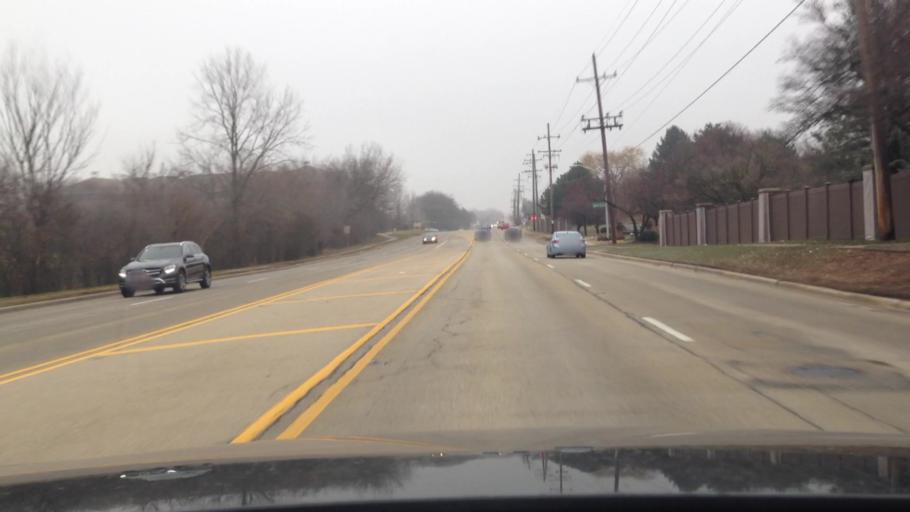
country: US
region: Illinois
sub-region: DuPage County
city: Westmont
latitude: 41.8191
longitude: -87.9764
